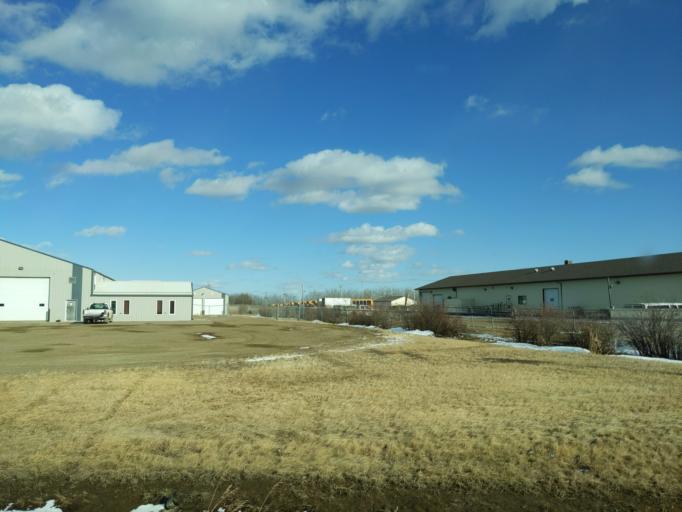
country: CA
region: Saskatchewan
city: Lloydminster
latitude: 53.2759
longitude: -109.9705
